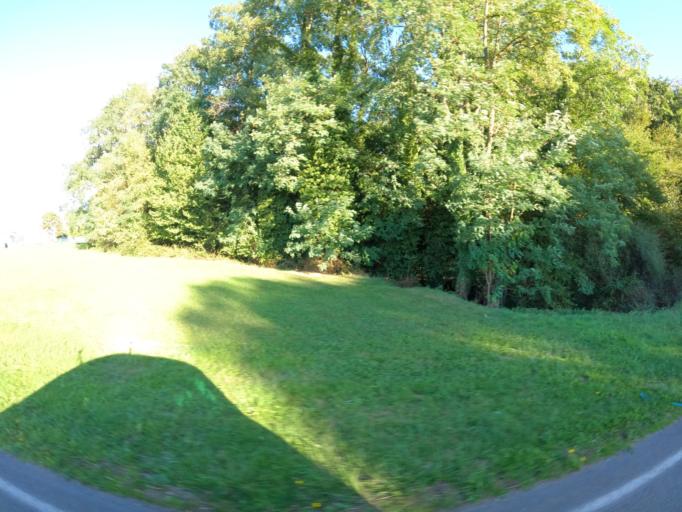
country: FR
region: Bourgogne
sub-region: Departement de Saone-et-Loire
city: Torcy
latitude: 46.7614
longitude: 4.4427
